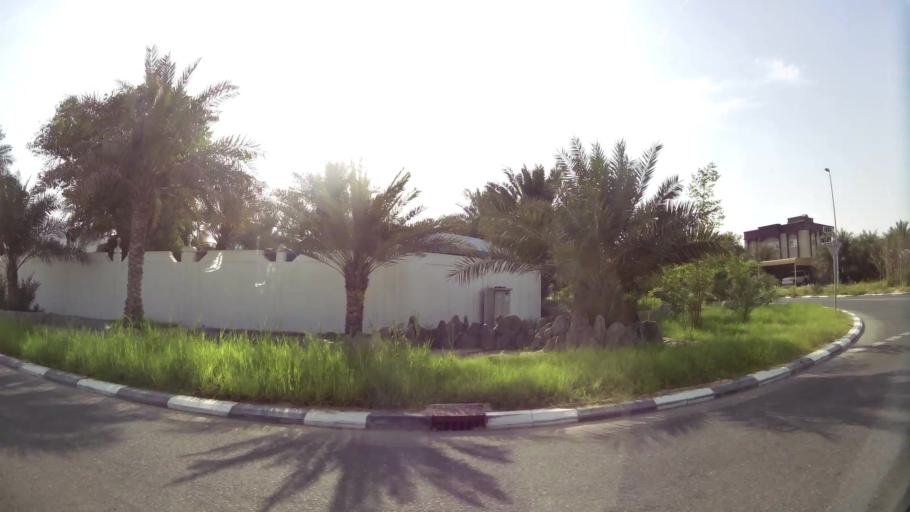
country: AE
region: Ash Shariqah
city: Sharjah
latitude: 25.2436
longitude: 55.4067
